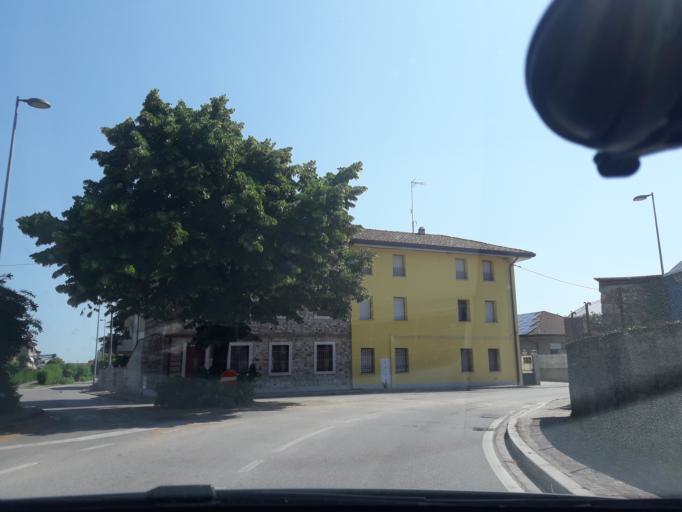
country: IT
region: Friuli Venezia Giulia
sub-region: Provincia di Udine
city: Tavagnacco
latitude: 46.1092
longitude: 13.2333
